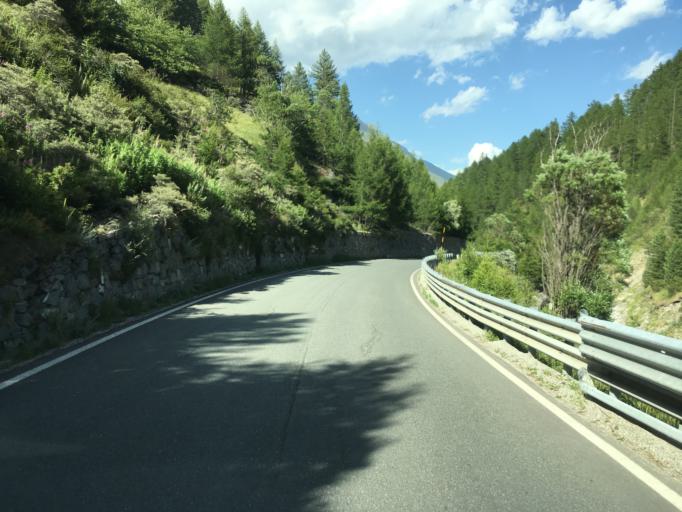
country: IT
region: Piedmont
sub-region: Provincia di Torino
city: Pragelato-Rua
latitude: 45.0254
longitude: 6.9531
